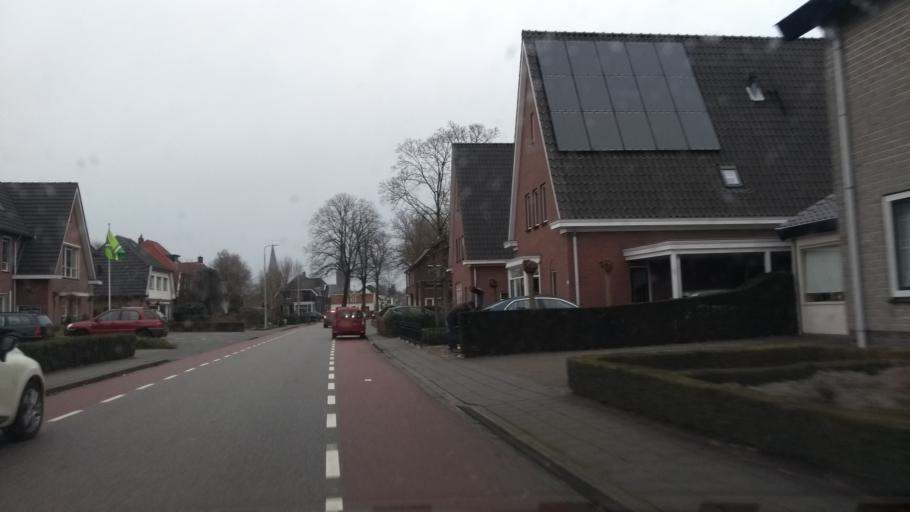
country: NL
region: Gelderland
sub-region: Gemeente Bronckhorst
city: Hengelo
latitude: 52.0471
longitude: 6.3082
